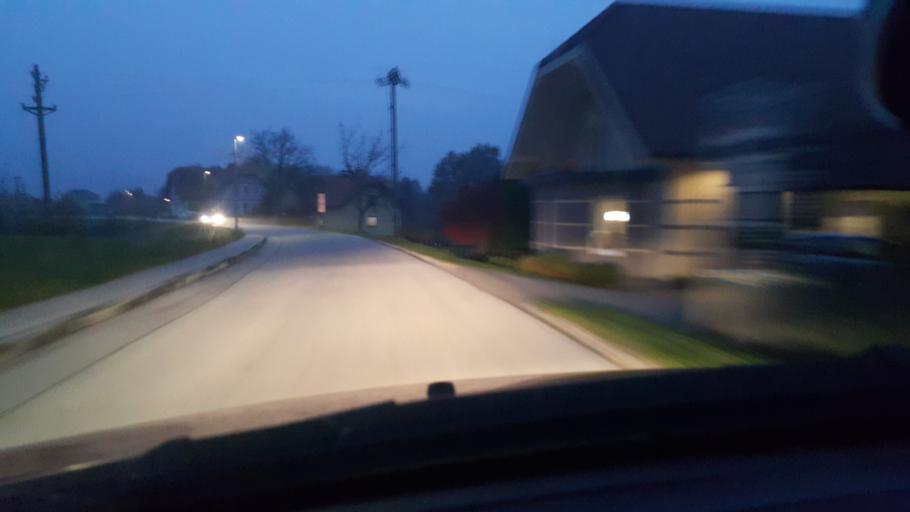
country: SI
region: Majsperk
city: Majsperk
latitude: 46.3528
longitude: 15.7604
